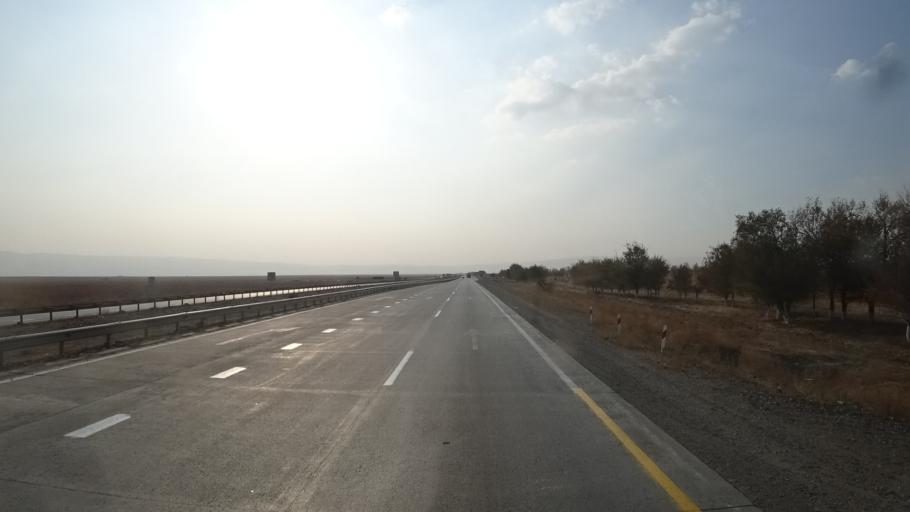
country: KZ
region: Zhambyl
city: Taraz
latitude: 42.8153
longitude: 71.1413
